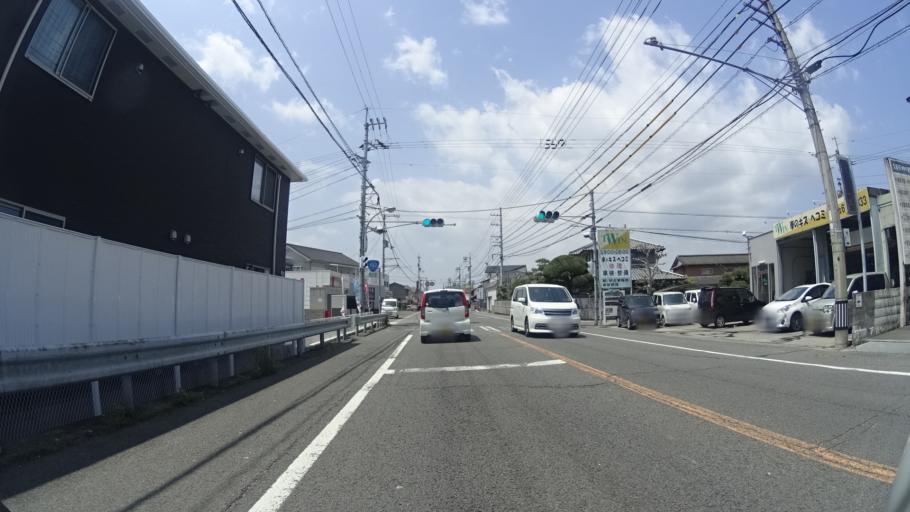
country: JP
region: Tokushima
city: Ishii
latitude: 34.0733
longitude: 134.4930
